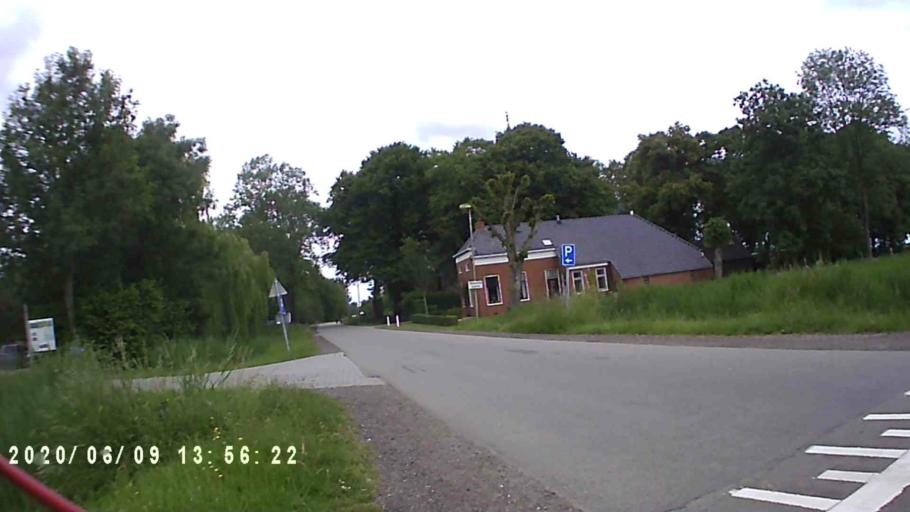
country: NL
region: Groningen
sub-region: Gemeente Groningen
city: Oosterpark
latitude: 53.2435
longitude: 6.6276
